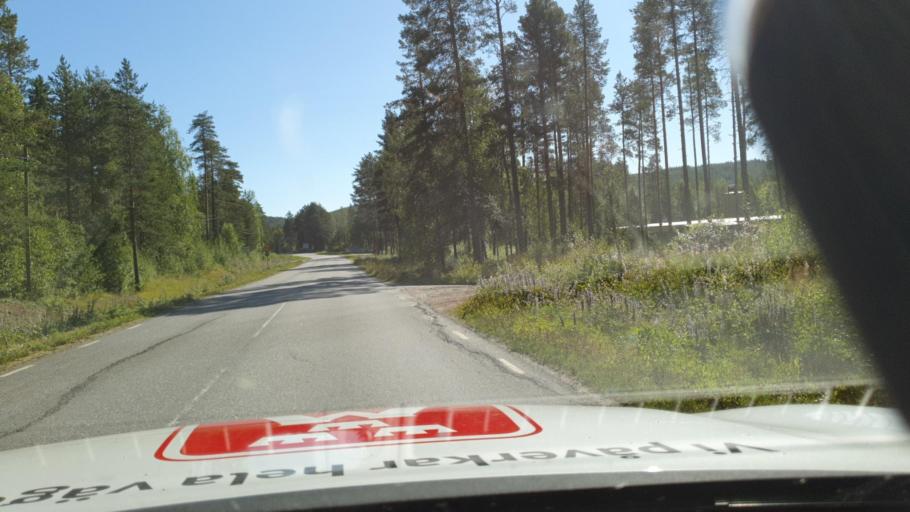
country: SE
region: Vaesterbotten
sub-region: Dorotea Kommun
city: Dorotea
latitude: 64.2608
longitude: 16.3726
